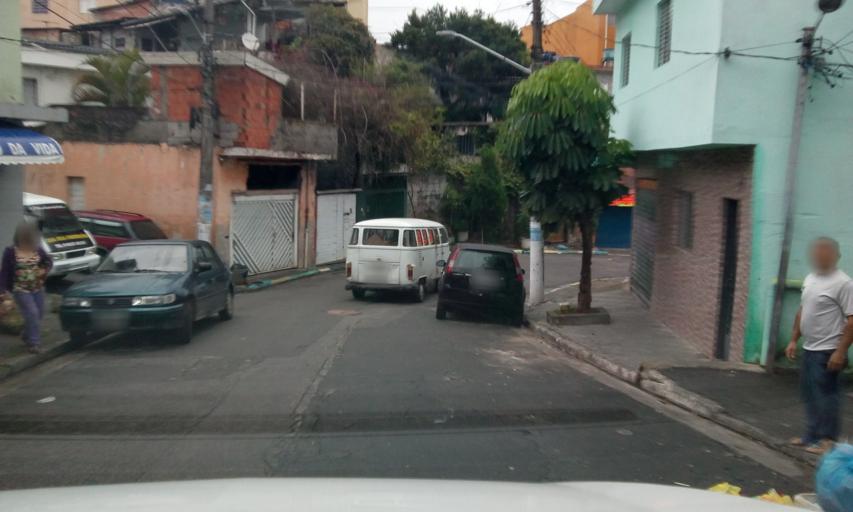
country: BR
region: Sao Paulo
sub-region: Diadema
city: Diadema
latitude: -23.6985
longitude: -46.6299
